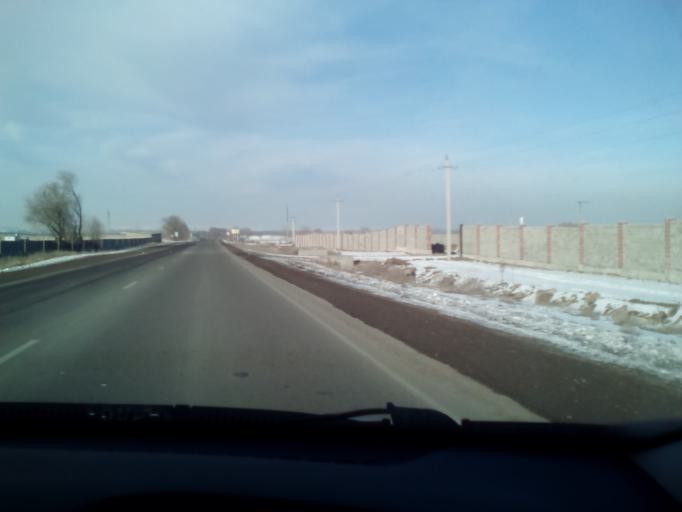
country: KZ
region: Almaty Oblysy
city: Burunday
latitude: 43.2039
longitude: 76.4149
